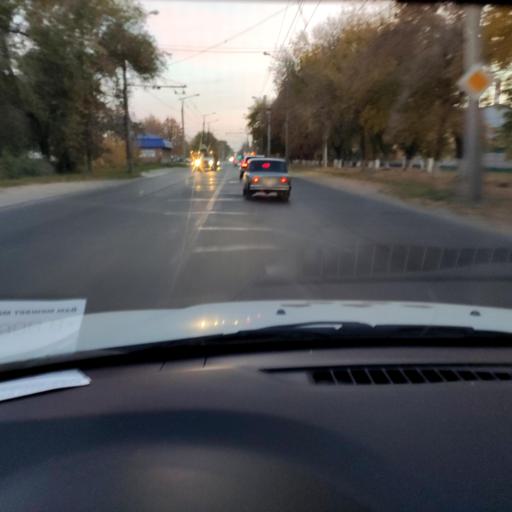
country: RU
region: Samara
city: Tol'yatti
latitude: 53.5392
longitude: 49.4426
